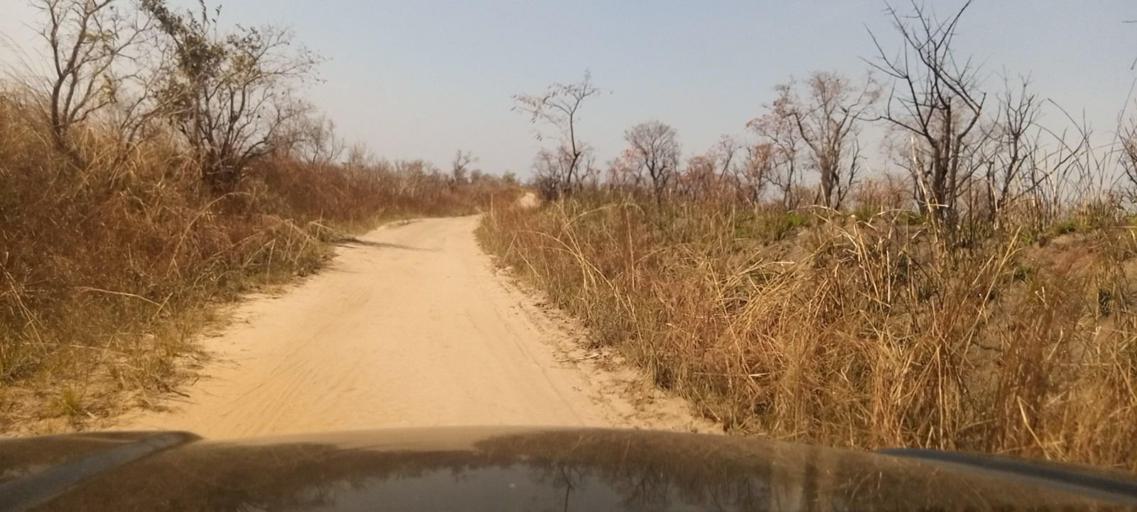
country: CD
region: Kasai-Oriental
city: Kabinda
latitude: -5.7936
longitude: 25.0364
